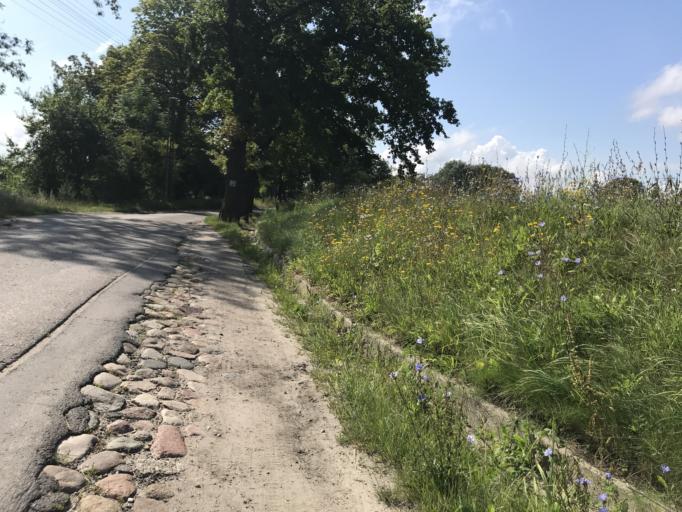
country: PL
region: Pomeranian Voivodeship
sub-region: Gdansk
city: Gdansk
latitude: 54.3330
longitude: 18.6572
